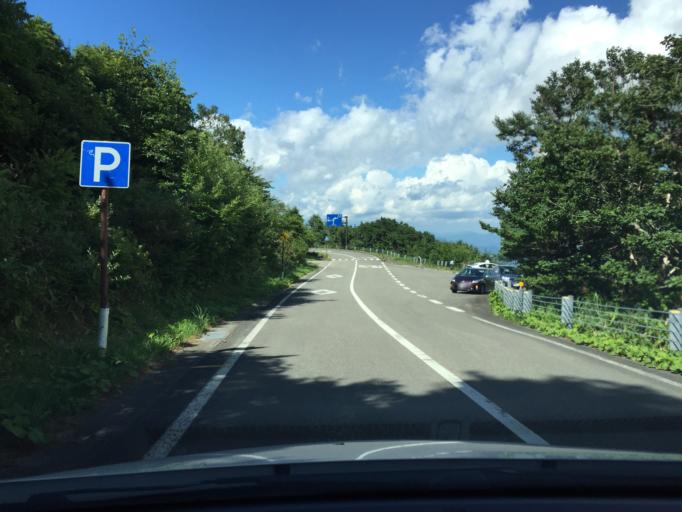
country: JP
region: Fukushima
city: Fukushima-shi
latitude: 37.7470
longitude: 140.2843
